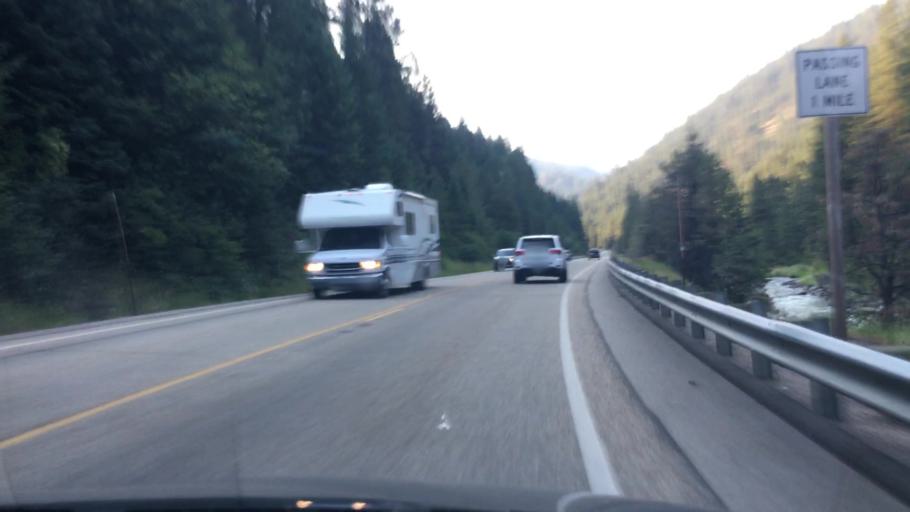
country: US
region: Idaho
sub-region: Valley County
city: Cascade
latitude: 44.1553
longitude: -116.1179
